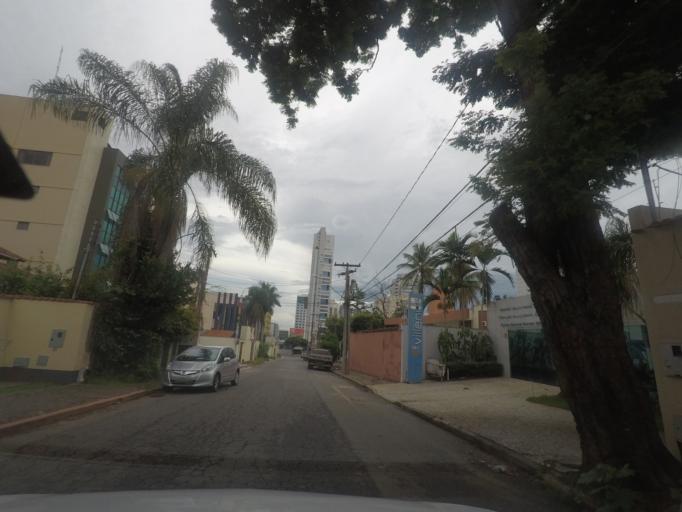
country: BR
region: Goias
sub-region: Goiania
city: Goiania
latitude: -16.6927
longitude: -49.2650
